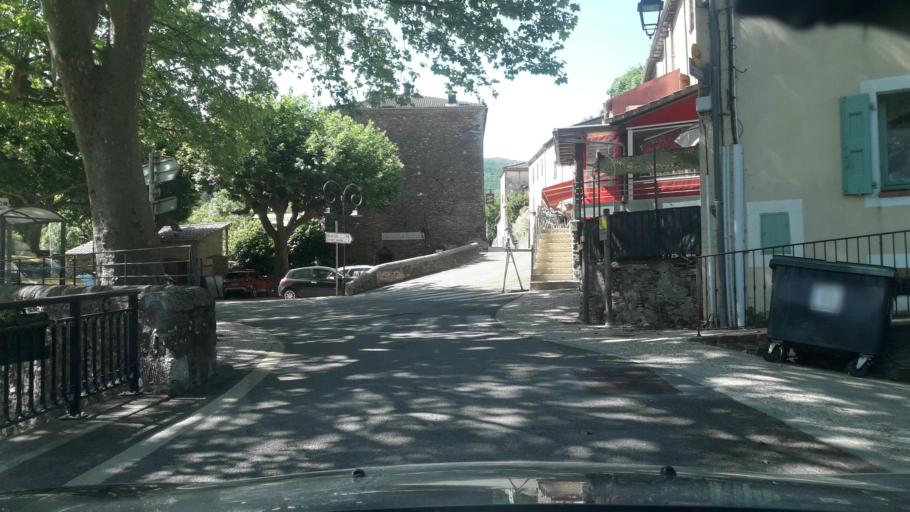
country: FR
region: Languedoc-Roussillon
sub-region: Departement du Gard
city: Valleraugue
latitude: 44.1172
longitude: 3.7231
